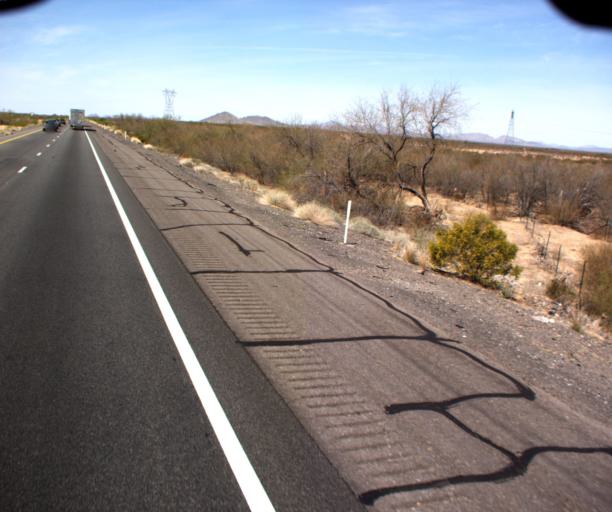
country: US
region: Arizona
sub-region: La Paz County
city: Salome
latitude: 33.5746
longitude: -113.3881
